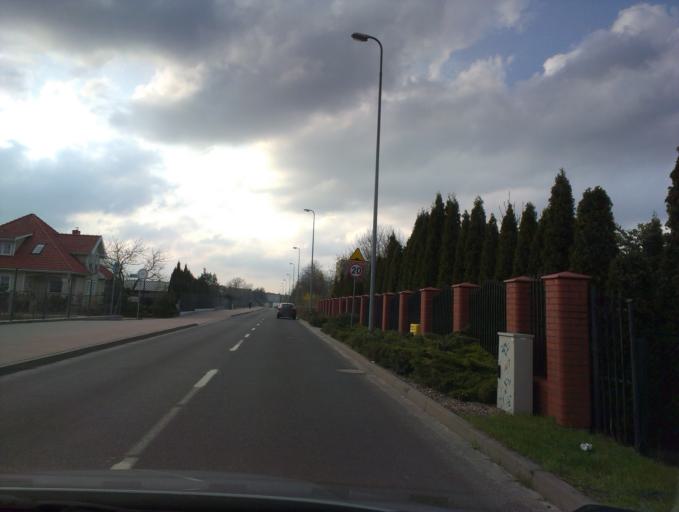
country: PL
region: West Pomeranian Voivodeship
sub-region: Powiat szczecinecki
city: Szczecinek
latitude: 53.7155
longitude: 16.6896
